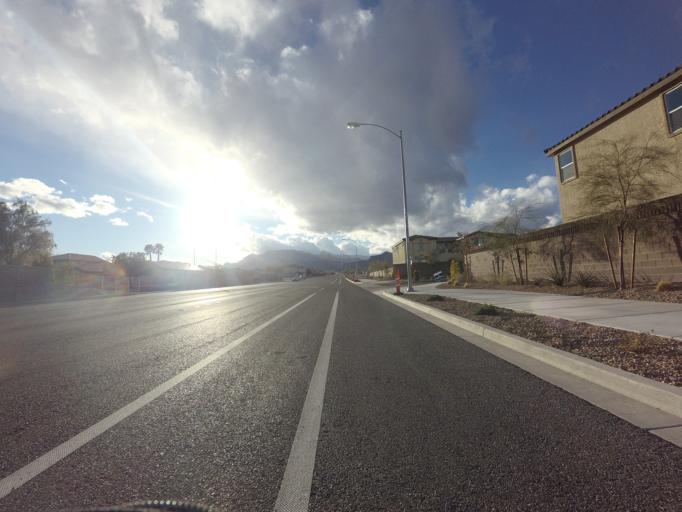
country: US
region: Nevada
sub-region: Clark County
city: Summerlin South
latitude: 36.2339
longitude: -115.2817
